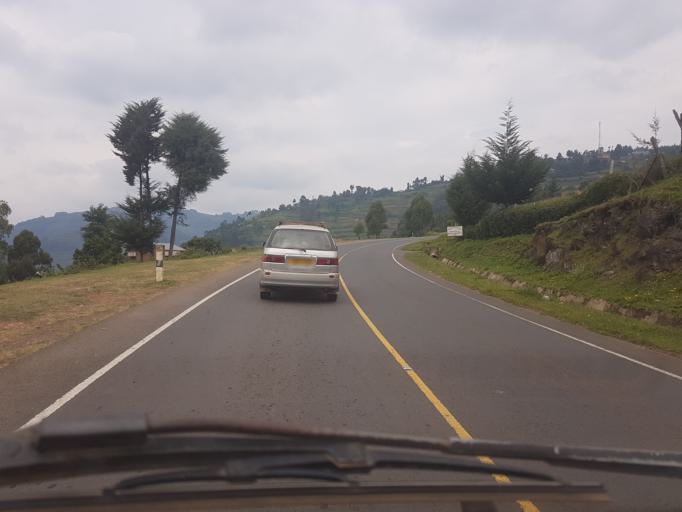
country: UG
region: Western Region
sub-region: Kisoro District
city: Kisoro
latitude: -1.2018
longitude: 29.8129
